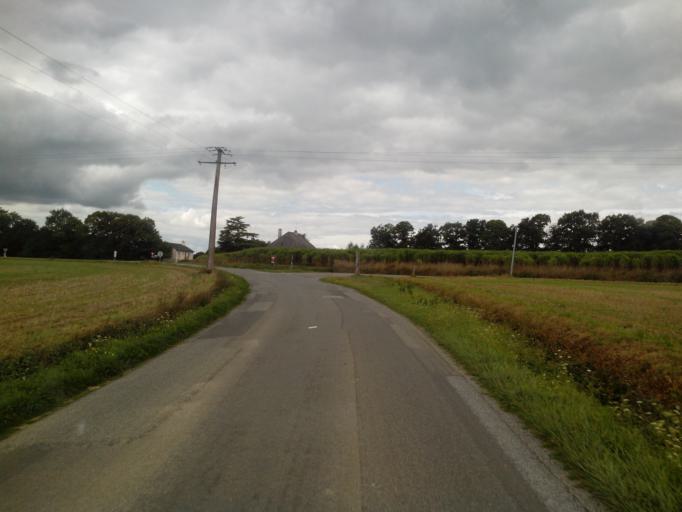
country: FR
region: Brittany
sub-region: Departement d'Ille-et-Vilaine
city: Noyal-sur-Vilaine
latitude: 48.1302
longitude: -1.5038
